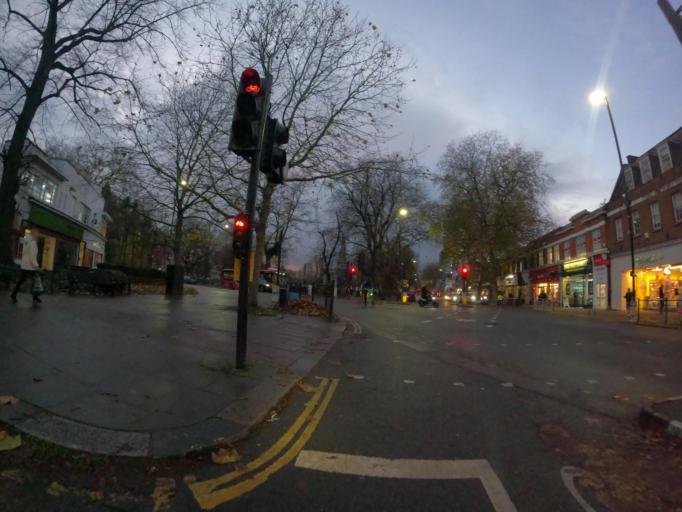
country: GB
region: England
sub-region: Greater London
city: Acton
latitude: 51.4925
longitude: -0.2625
